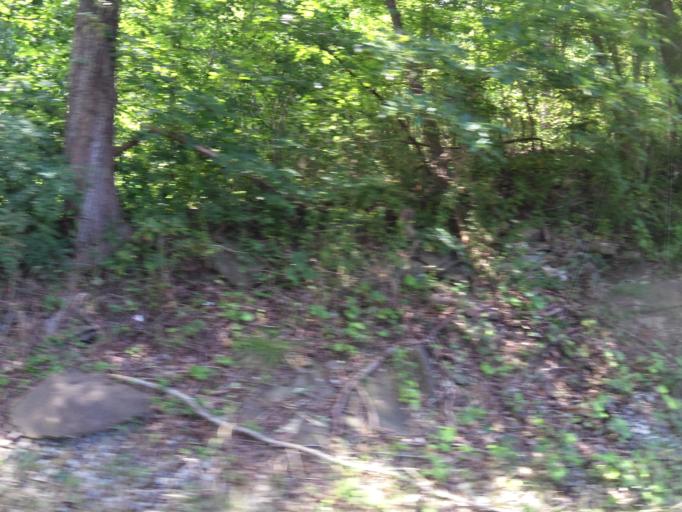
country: US
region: Kentucky
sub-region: Harlan County
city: Harlan
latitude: 36.8970
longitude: -83.3103
